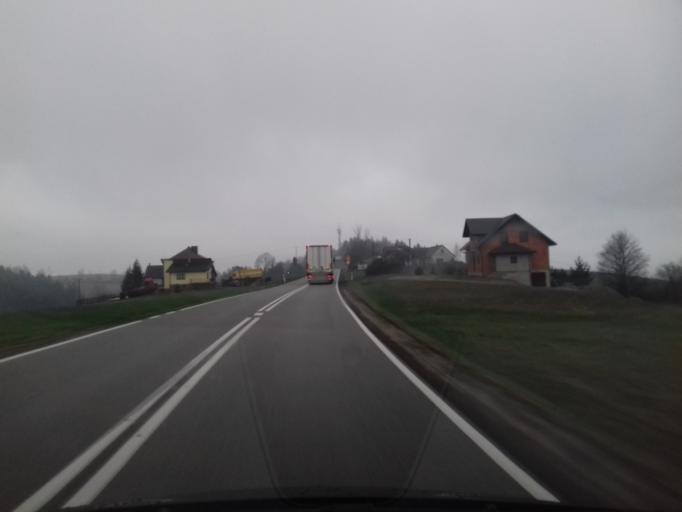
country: PL
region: Lesser Poland Voivodeship
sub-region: Powiat nowosadecki
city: Podegrodzie
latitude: 49.6534
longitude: 20.5672
